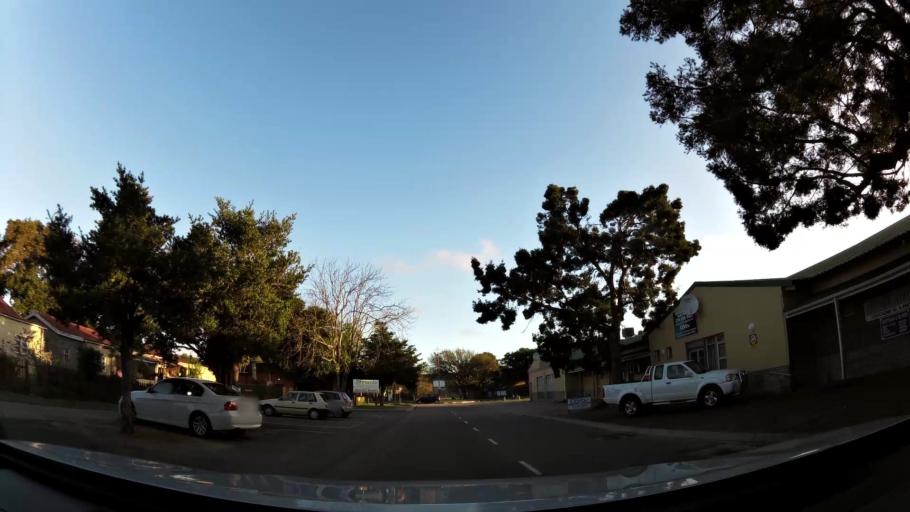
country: ZA
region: Western Cape
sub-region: Eden District Municipality
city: Knysna
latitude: -34.0151
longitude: 22.8024
